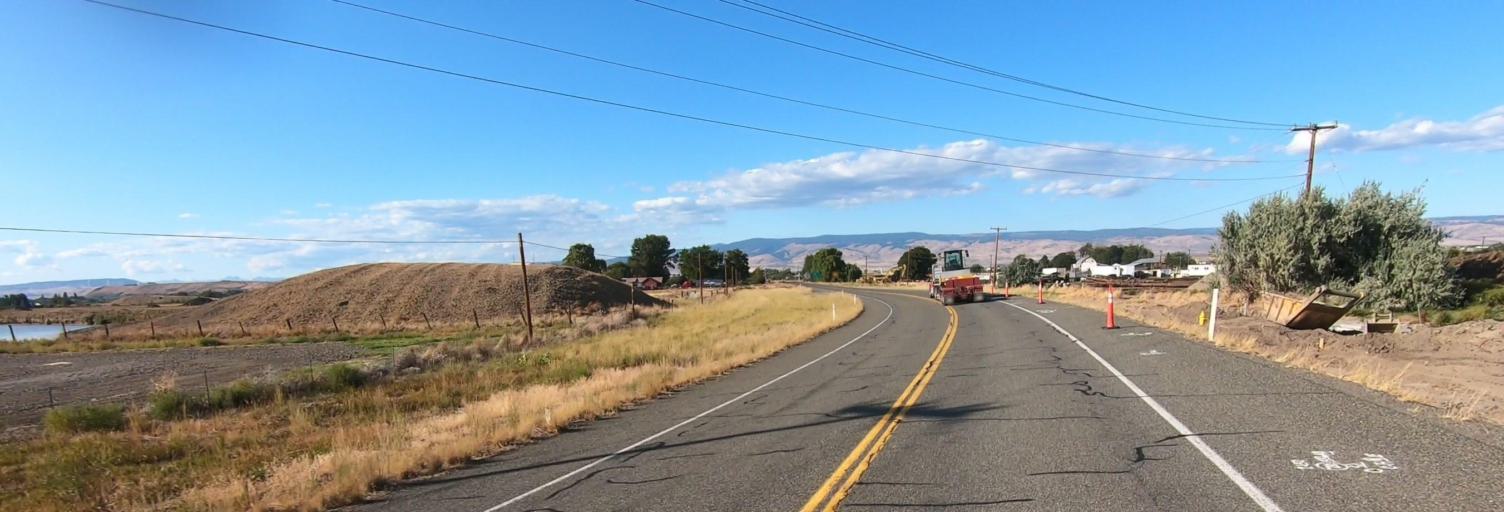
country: US
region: Washington
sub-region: Kittitas County
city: Ellensburg
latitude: 47.0163
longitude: -120.5954
